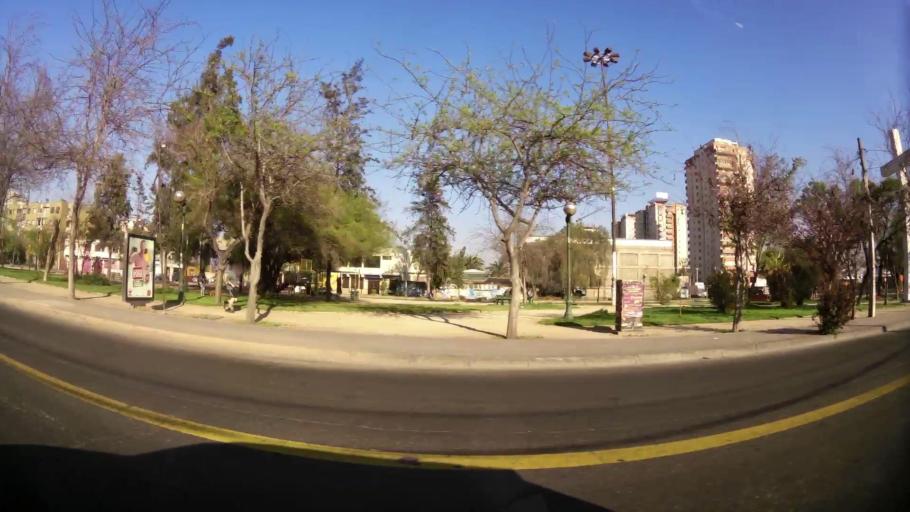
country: CL
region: Santiago Metropolitan
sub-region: Provincia de Santiago
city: Santiago
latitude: -33.4782
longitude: -70.6483
